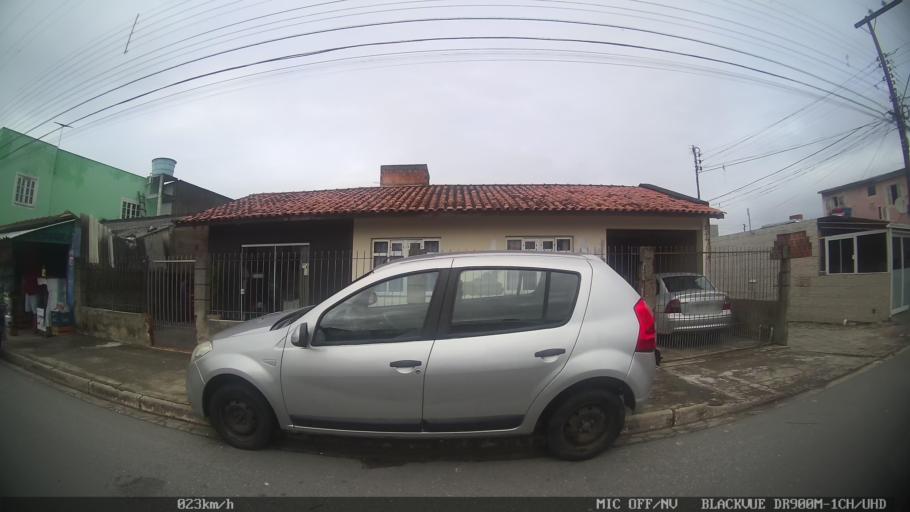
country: BR
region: Santa Catarina
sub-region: Biguacu
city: Biguacu
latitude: -27.5393
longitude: -48.6422
